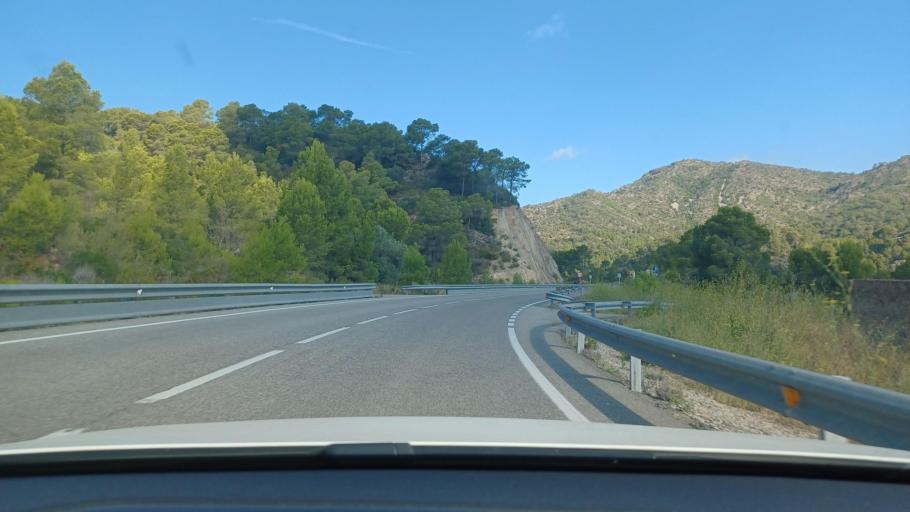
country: ES
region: Catalonia
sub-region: Provincia de Tarragona
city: Benifallet
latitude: 40.9490
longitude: 0.4584
